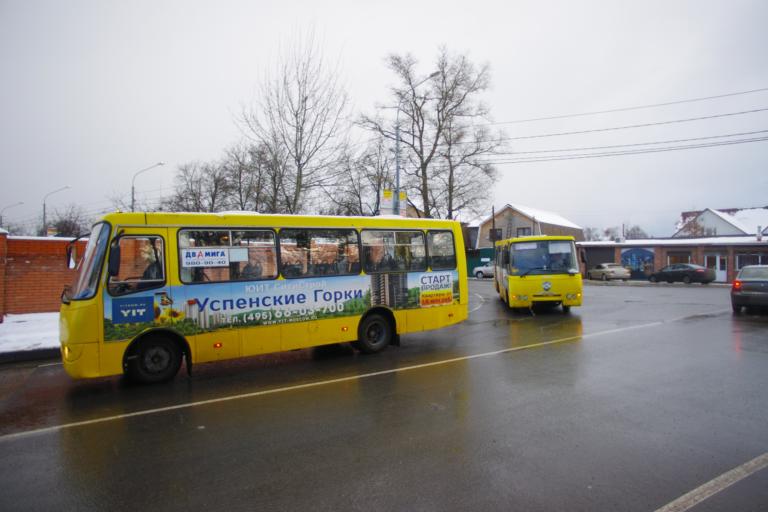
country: RU
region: Moskovskaya
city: Arkhangel'skoye
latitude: 55.7996
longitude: 37.3071
